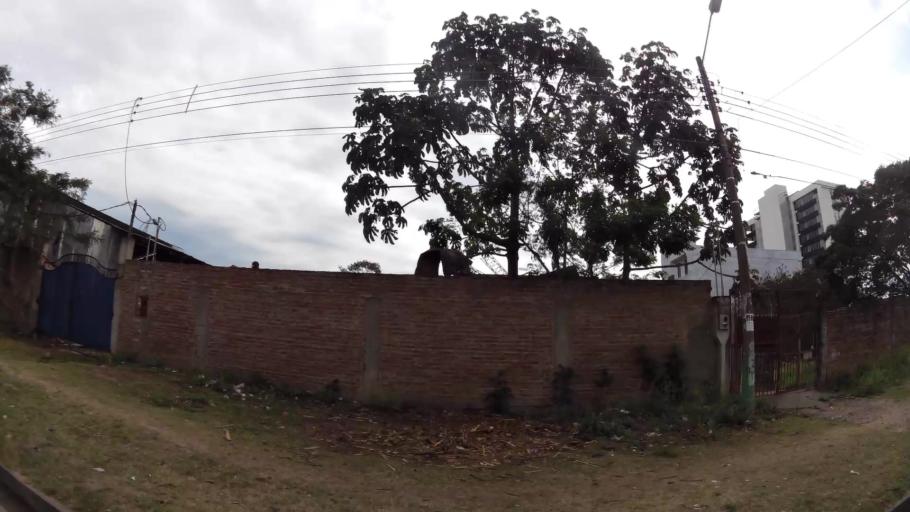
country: BO
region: Santa Cruz
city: Santa Cruz de la Sierra
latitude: -17.7798
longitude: -63.2150
